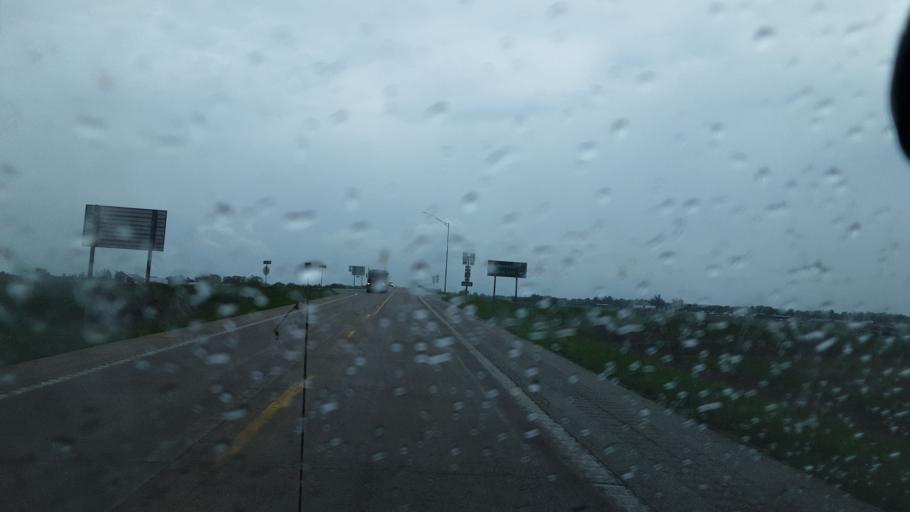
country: US
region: Missouri
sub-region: Marion County
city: Palmyra
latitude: 39.7000
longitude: -91.5069
